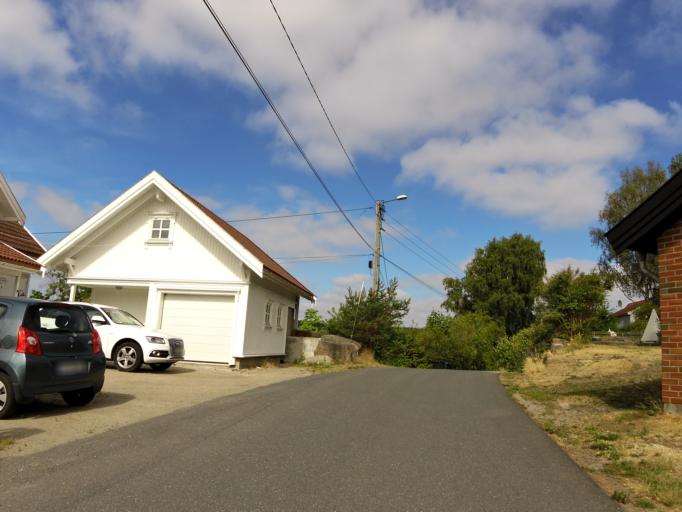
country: NO
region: Ostfold
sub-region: Fredrikstad
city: Fredrikstad
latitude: 59.2370
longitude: 10.9172
